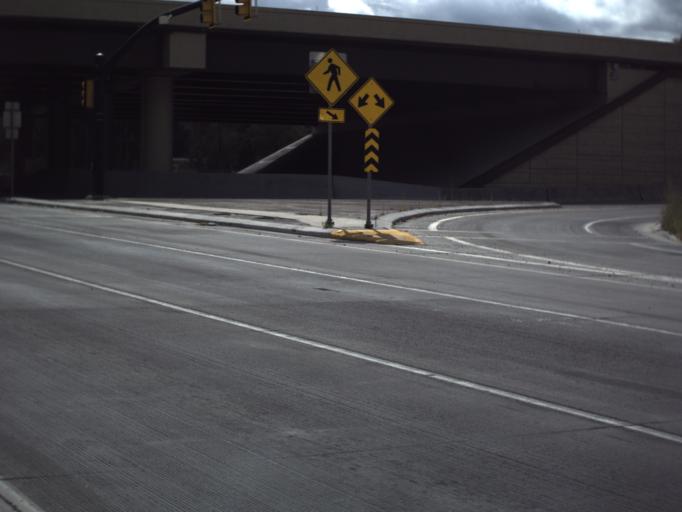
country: US
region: Utah
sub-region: Salt Lake County
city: Bluffdale
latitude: 40.5014
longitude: -111.9387
